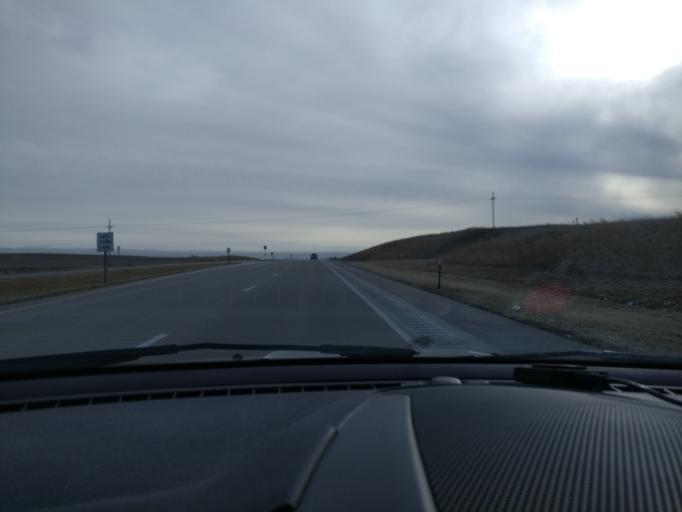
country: US
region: Nebraska
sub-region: Saunders County
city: Wahoo
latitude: 41.1632
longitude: -96.6314
